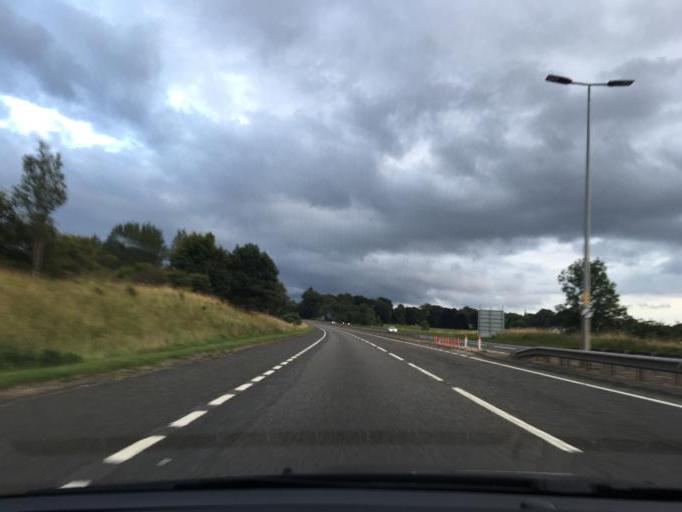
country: GB
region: Scotland
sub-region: Highland
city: Inverness
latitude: 57.4701
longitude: -4.1825
